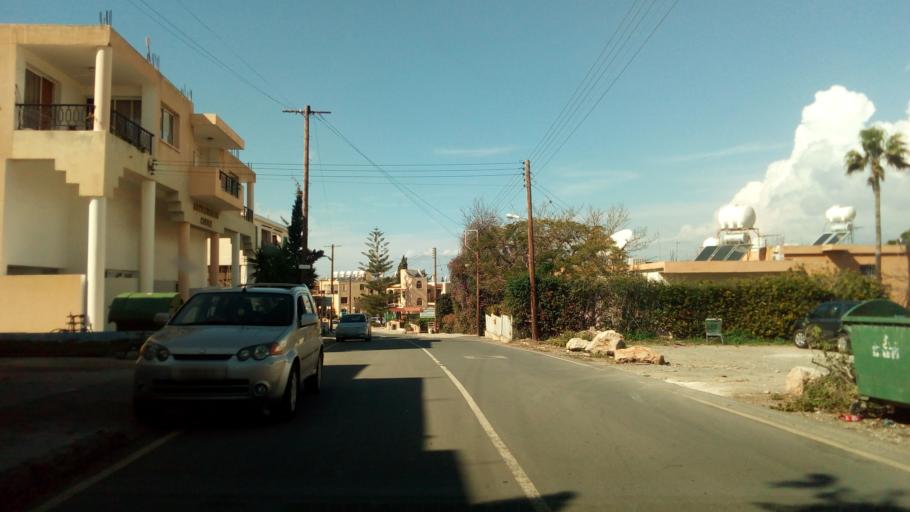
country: CY
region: Pafos
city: Chlorakas
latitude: 34.8030
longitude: 32.4058
